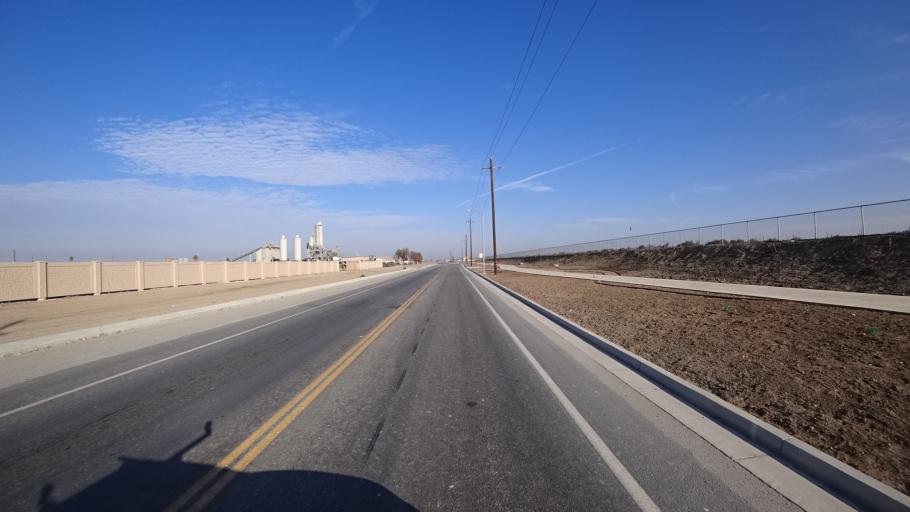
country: US
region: California
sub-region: Kern County
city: Greenfield
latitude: 35.2788
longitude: -119.0922
